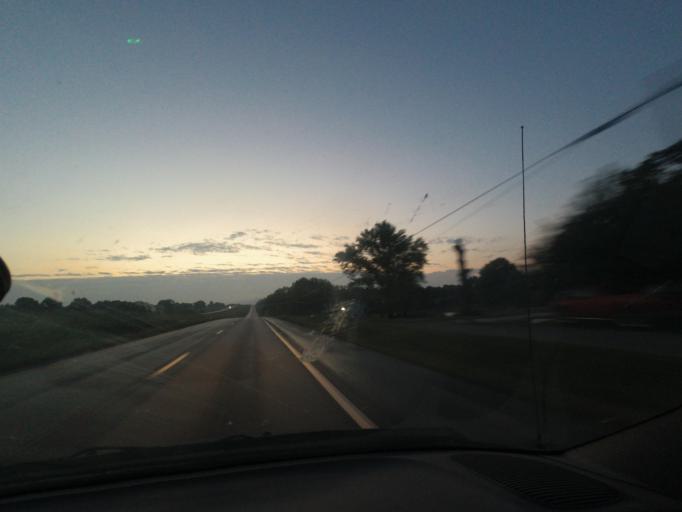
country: US
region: Missouri
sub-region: Linn County
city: Brookfield
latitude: 39.7794
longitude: -93.1269
